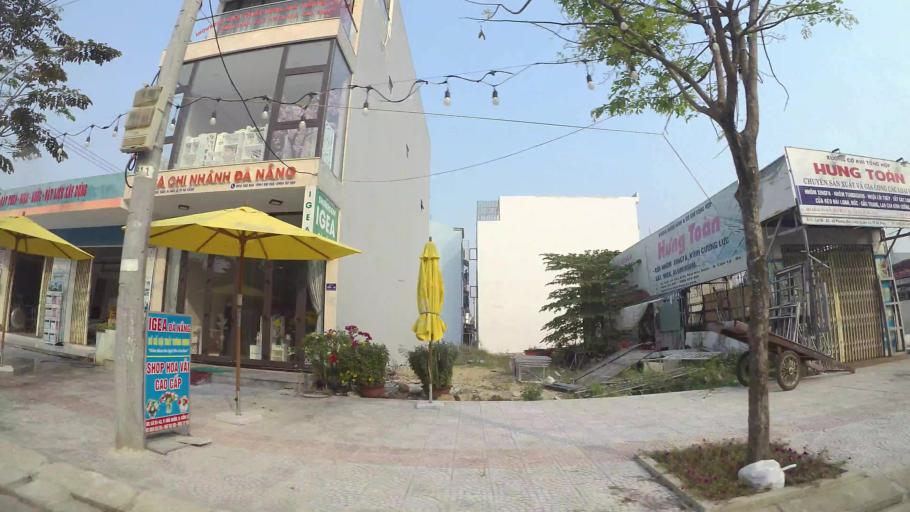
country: VN
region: Da Nang
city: Cam Le
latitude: 16.0125
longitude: 108.2191
